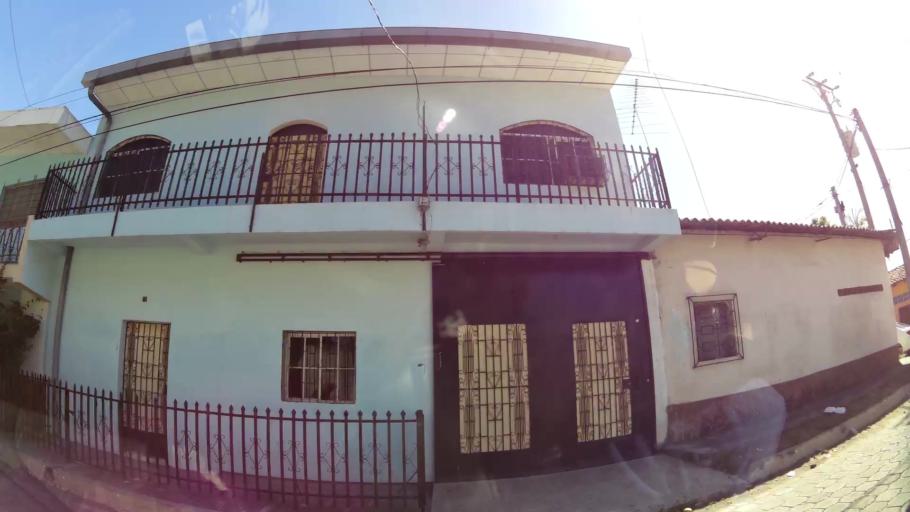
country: SV
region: San Miguel
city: San Miguel
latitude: 13.4932
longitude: -88.1710
